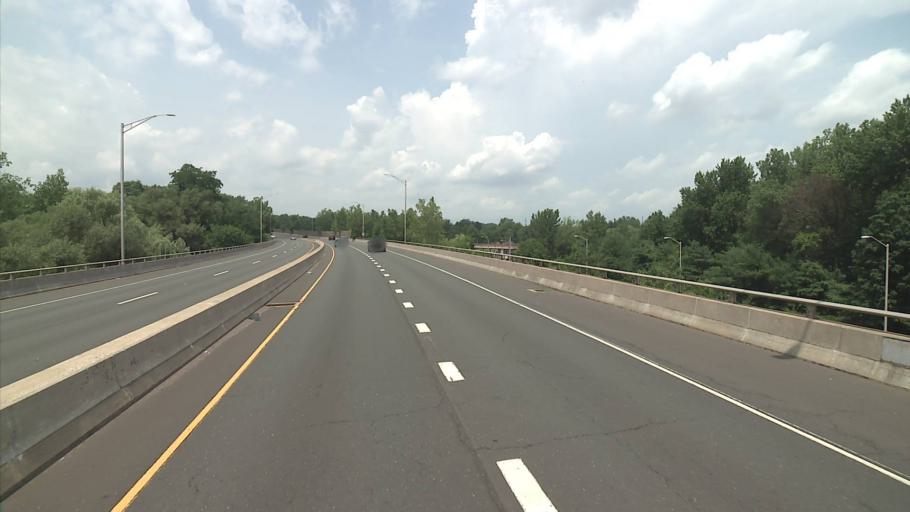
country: US
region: Connecticut
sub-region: Hartford County
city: South Windsor
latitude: 41.8176
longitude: -72.6557
